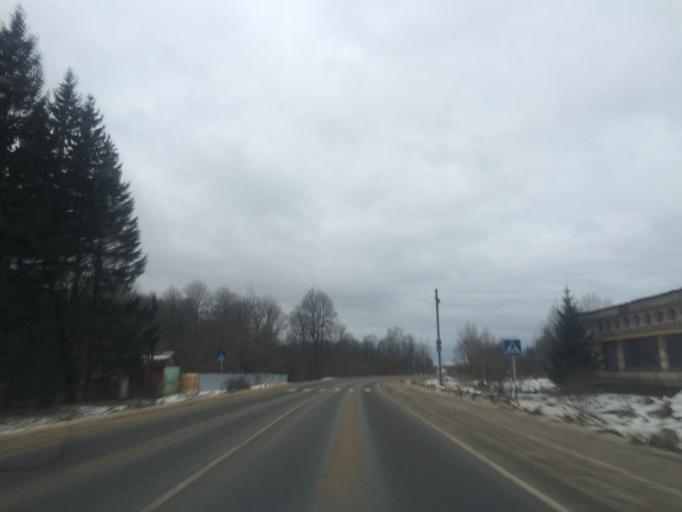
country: RU
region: Tula
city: Odoyev
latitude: 54.0074
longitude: 36.7788
